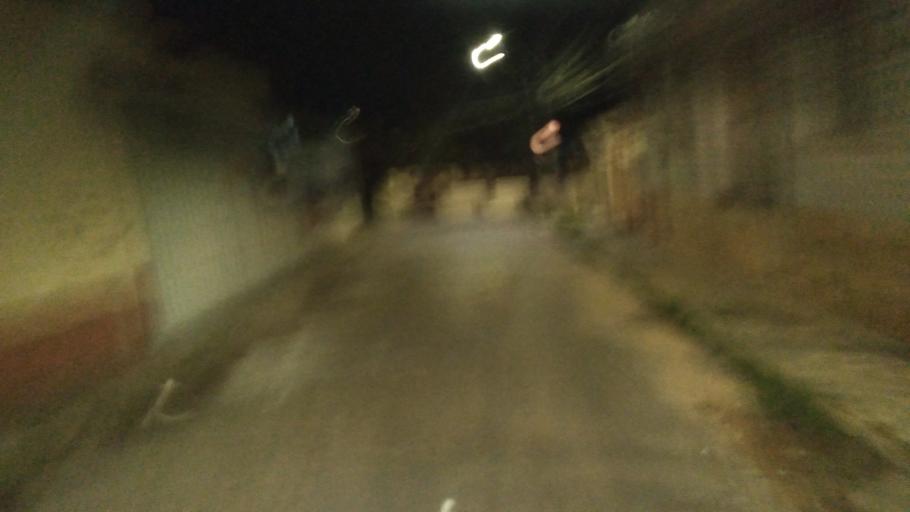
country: BR
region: Minas Gerais
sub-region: Belo Horizonte
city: Belo Horizonte
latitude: -19.9100
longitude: -43.9477
